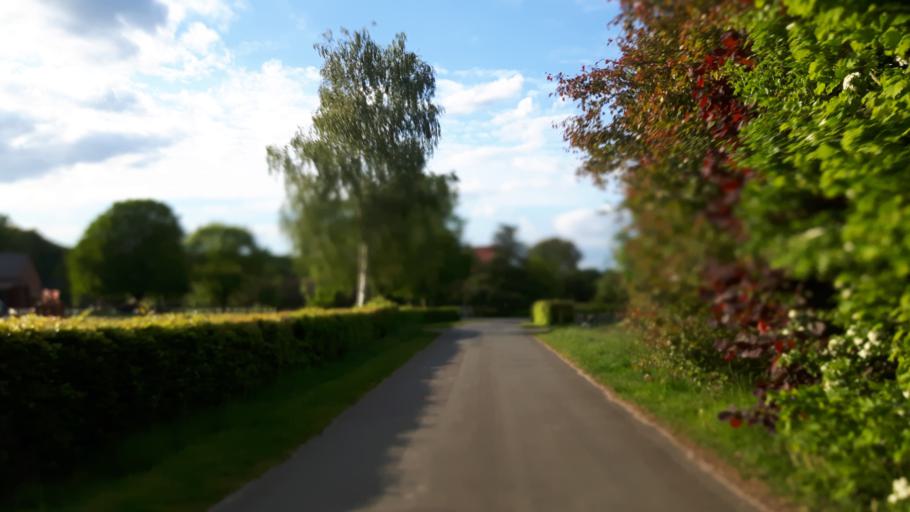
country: DE
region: Lower Saxony
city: Ganderkesee
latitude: 53.0273
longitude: 8.5831
